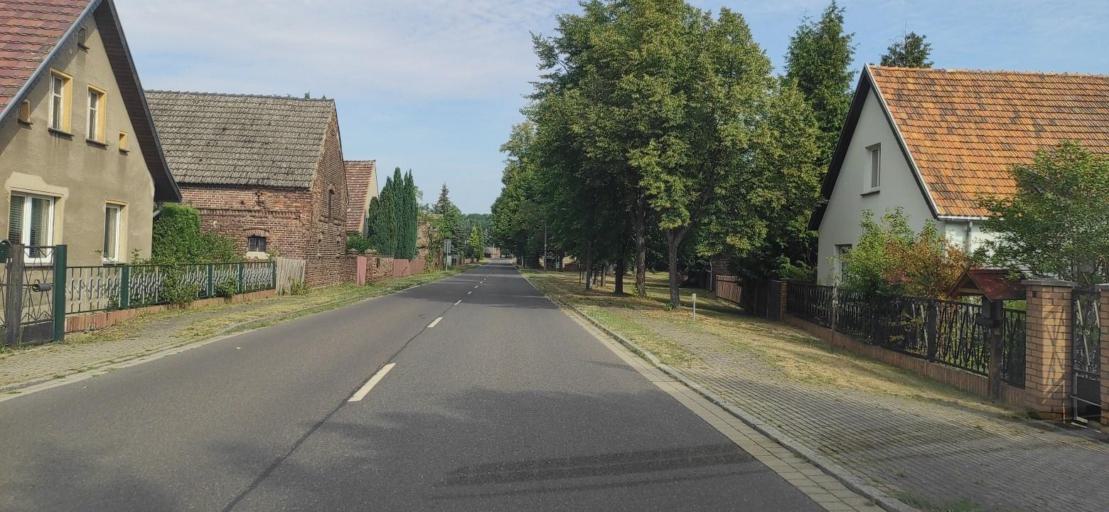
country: DE
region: Brandenburg
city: Forst
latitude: 51.6901
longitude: 14.7176
